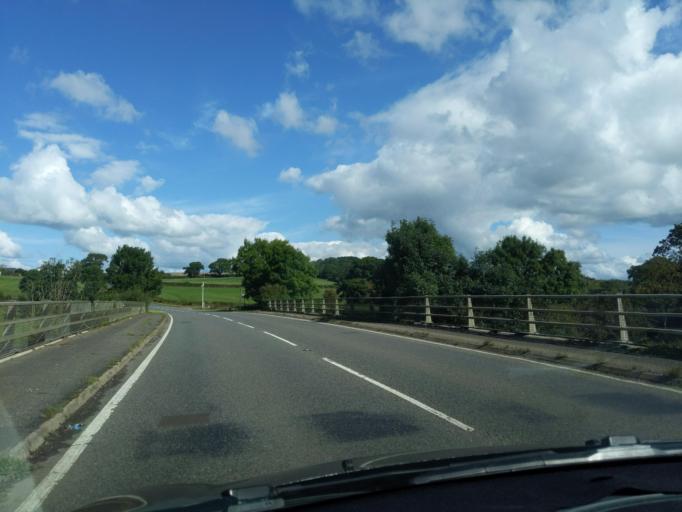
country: GB
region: England
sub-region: Cornwall
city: Launceston
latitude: 50.6567
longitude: -4.3381
